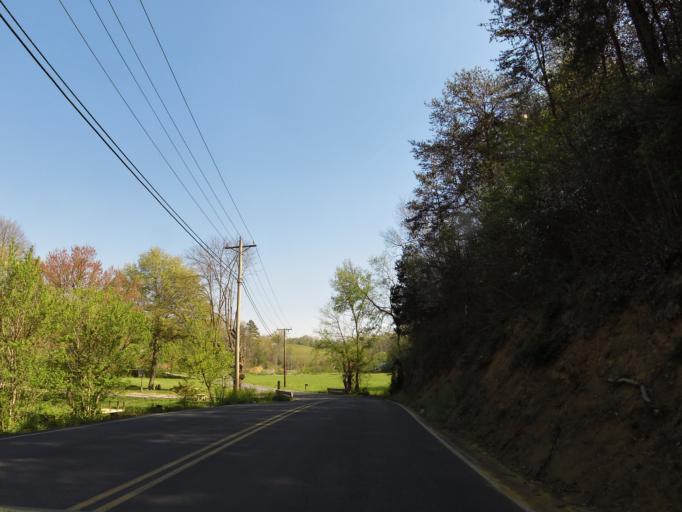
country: US
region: Tennessee
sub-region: Sevier County
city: Sevierville
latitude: 35.8497
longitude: -83.6352
